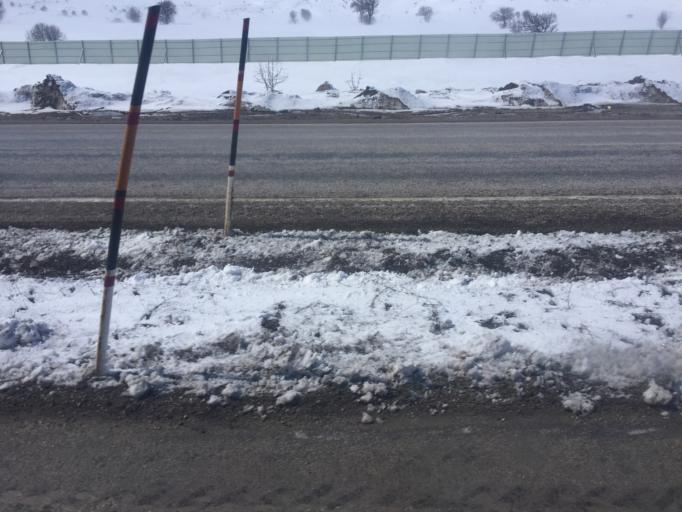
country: TR
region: Kahramanmaras
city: Goksun
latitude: 38.1750
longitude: 36.4608
